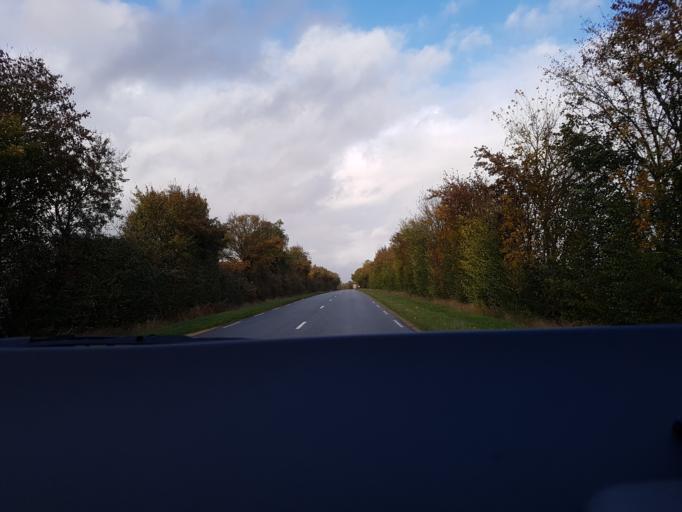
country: FR
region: Poitou-Charentes
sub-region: Departement des Deux-Sevres
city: Brioux-sur-Boutonne
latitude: 46.1305
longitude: -0.2294
